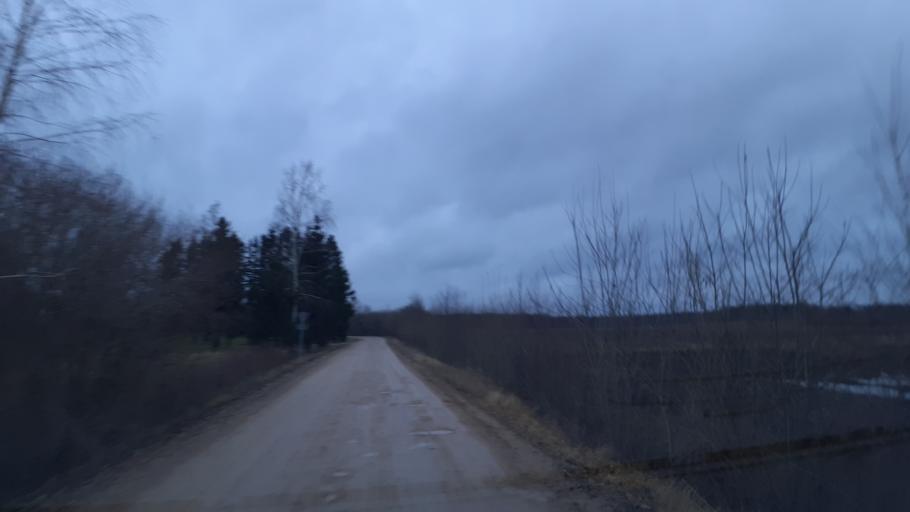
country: LV
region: Kuldigas Rajons
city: Kuldiga
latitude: 57.0430
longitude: 22.1355
